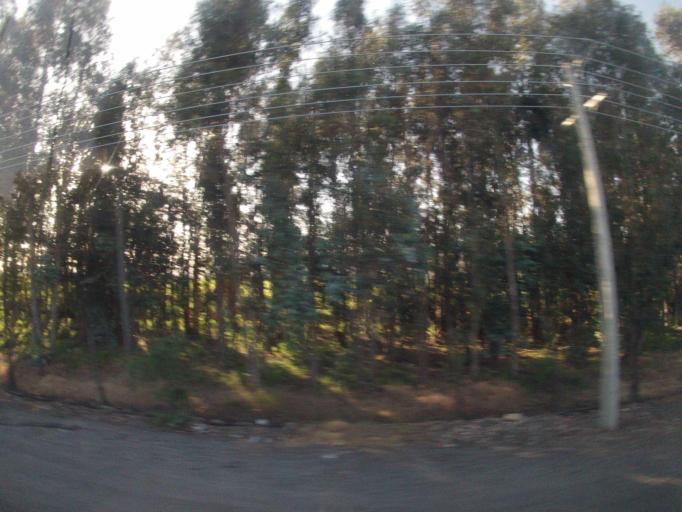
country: CL
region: O'Higgins
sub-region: Provincia de Colchagua
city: Chimbarongo
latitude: -34.7237
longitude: -71.0348
